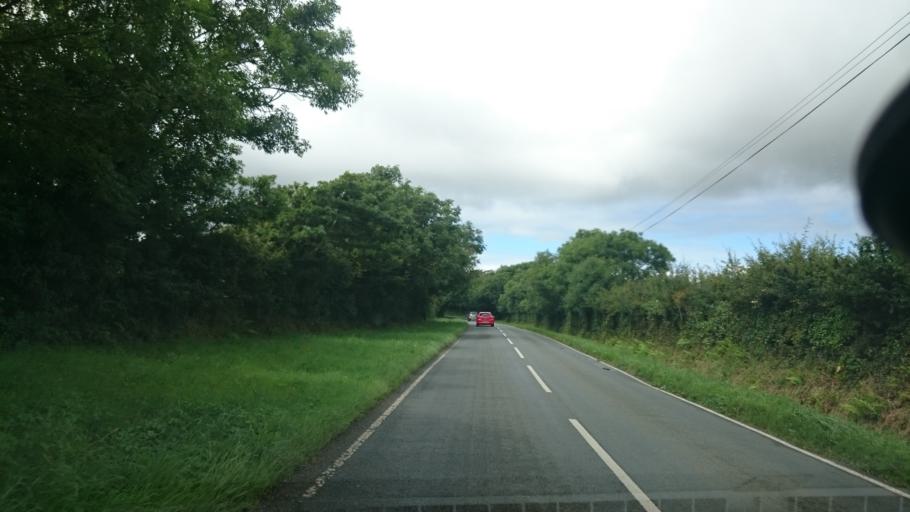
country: GB
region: Wales
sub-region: Pembrokeshire
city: Freystrop
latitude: 51.7439
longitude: -4.9459
